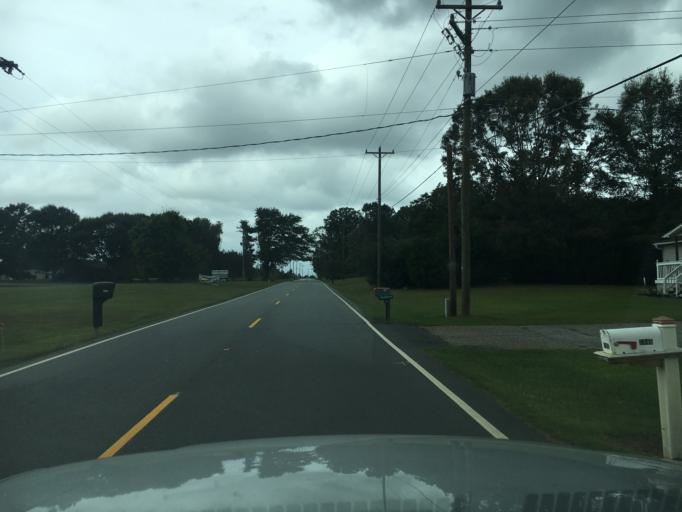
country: US
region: South Carolina
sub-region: Spartanburg County
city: Duncan
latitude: 34.8705
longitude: -82.1182
